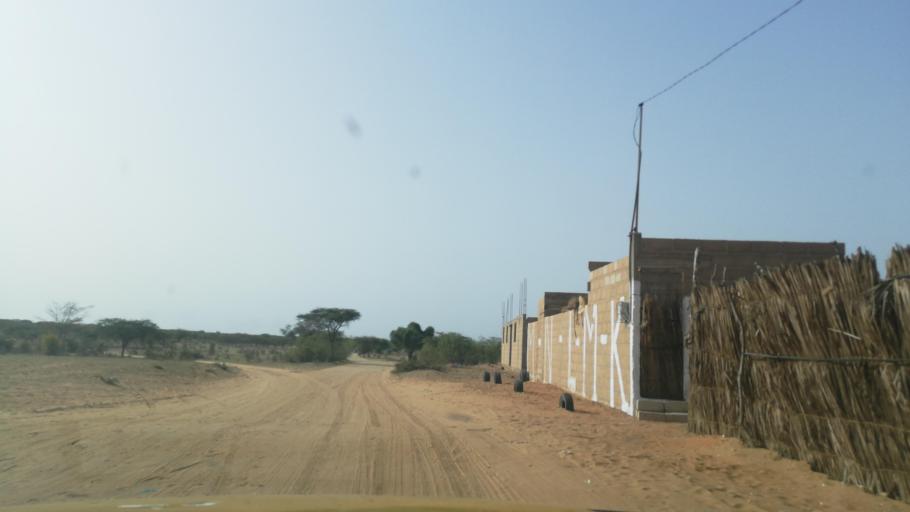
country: SN
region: Saint-Louis
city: Saint-Louis
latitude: 16.0569
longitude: -16.3323
